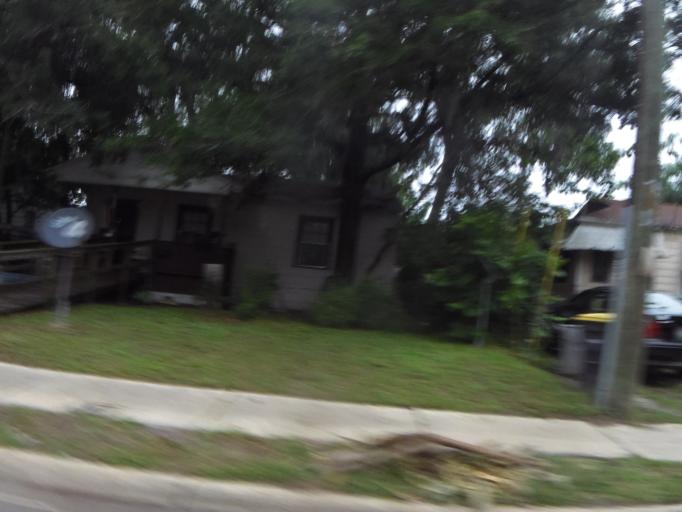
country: US
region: Florida
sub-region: Duval County
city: Jacksonville
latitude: 30.3487
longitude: -81.6331
